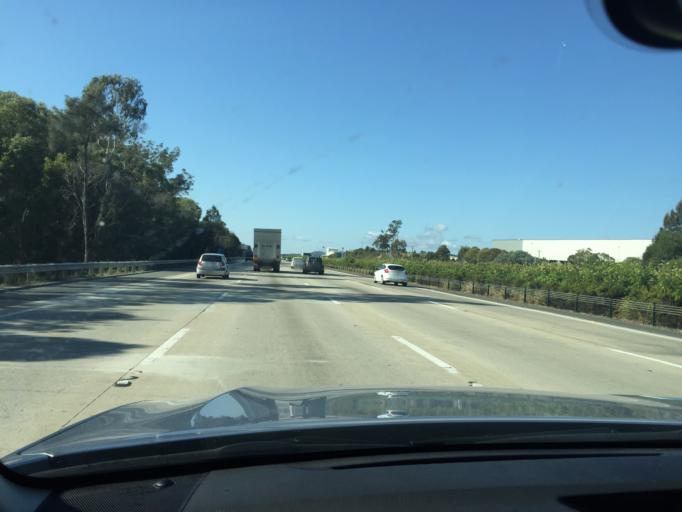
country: AU
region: Queensland
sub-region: Gold Coast
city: Yatala
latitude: -27.7437
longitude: 153.2330
